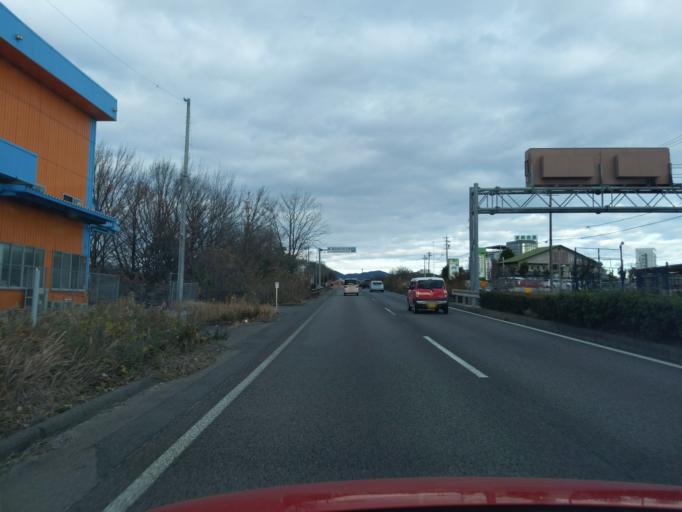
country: JP
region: Aichi
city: Kasugai
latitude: 35.2751
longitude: 137.0069
